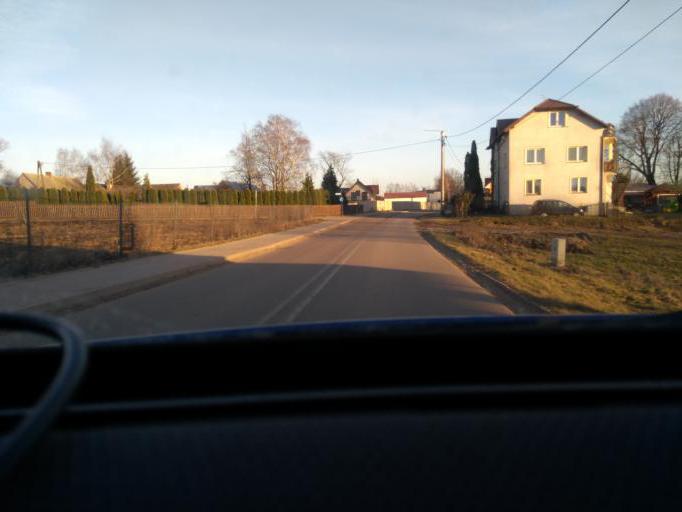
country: PL
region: Pomeranian Voivodeship
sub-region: Powiat kartuski
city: Przodkowo
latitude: 54.4114
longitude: 18.3234
